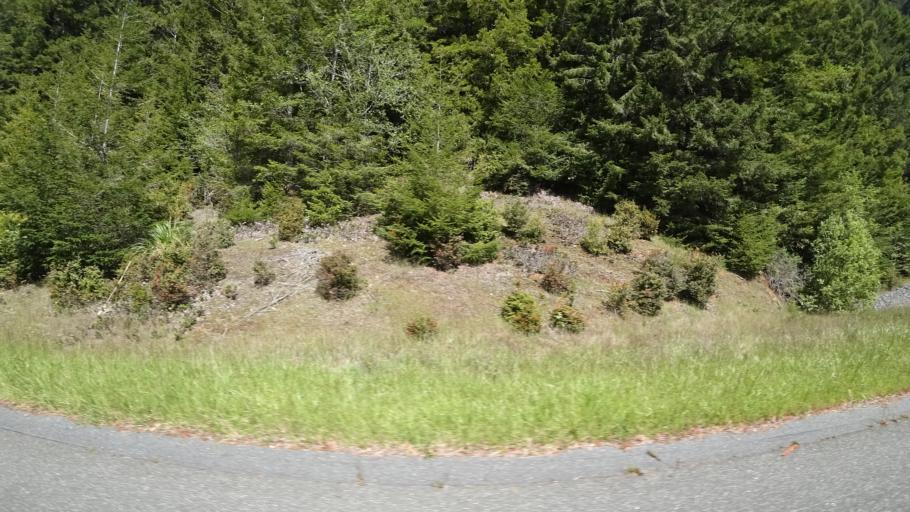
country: US
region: California
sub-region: Humboldt County
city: Westhaven-Moonstone
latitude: 41.3539
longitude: -124.0162
